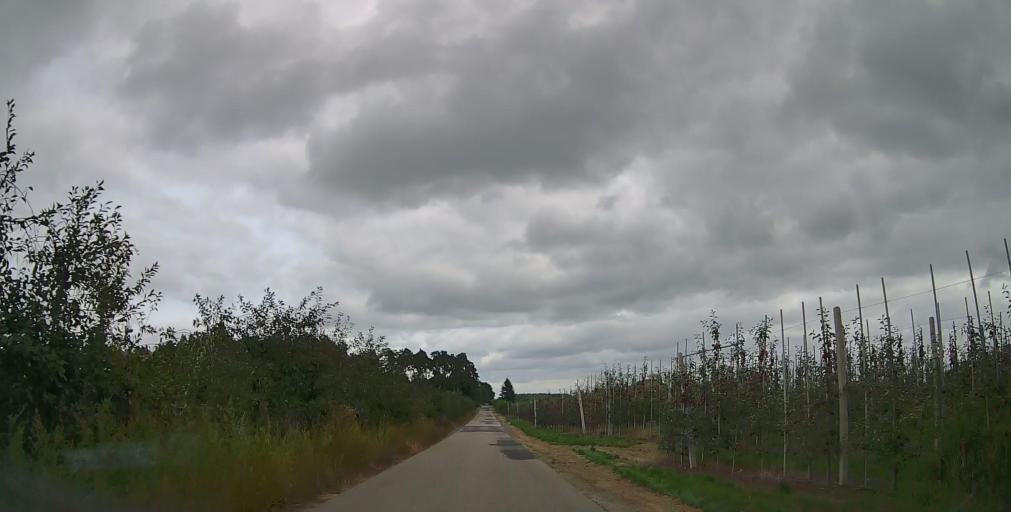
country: PL
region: Masovian Voivodeship
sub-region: Powiat grojecki
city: Goszczyn
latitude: 51.7749
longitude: 20.8587
